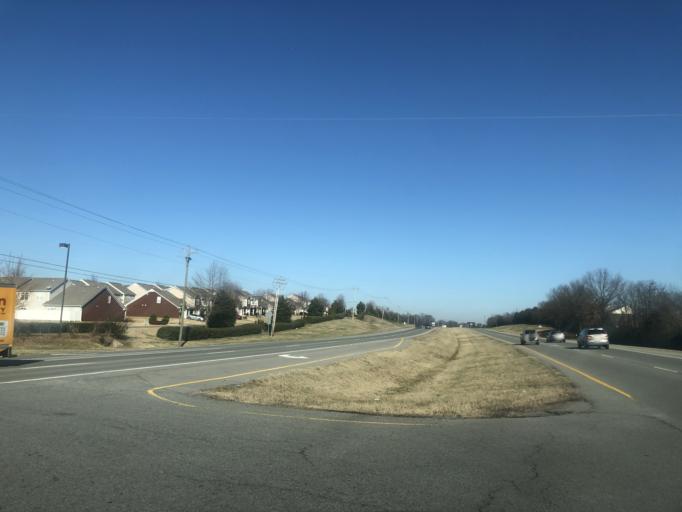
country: US
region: Tennessee
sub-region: Rutherford County
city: Smyrna
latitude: 35.9415
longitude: -86.5256
